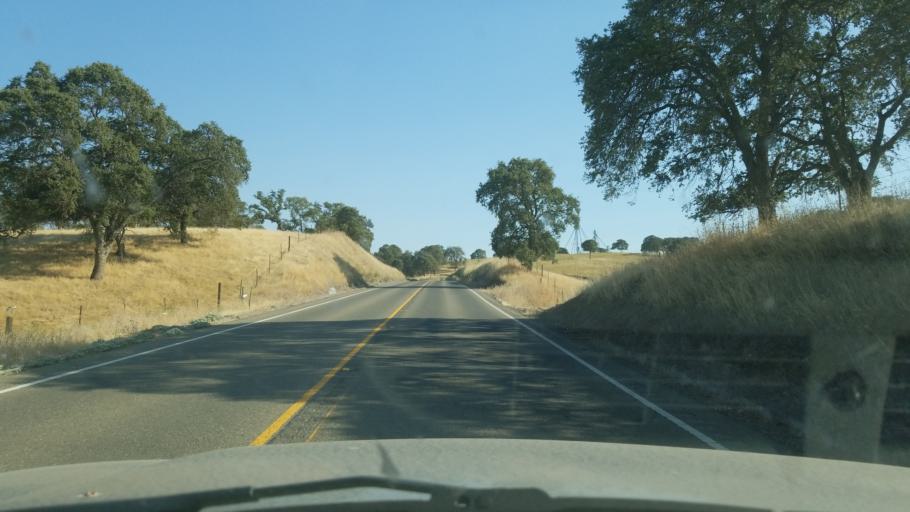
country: US
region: California
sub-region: Tuolumne County
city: Jamestown
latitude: 37.8231
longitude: -120.4739
